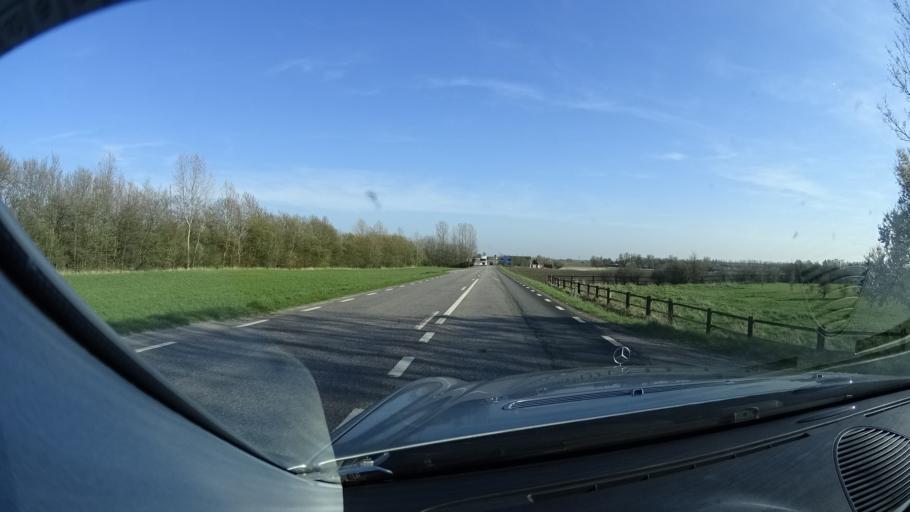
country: SE
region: Skane
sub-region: Landskrona
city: Asmundtorp
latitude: 55.8948
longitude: 12.9624
